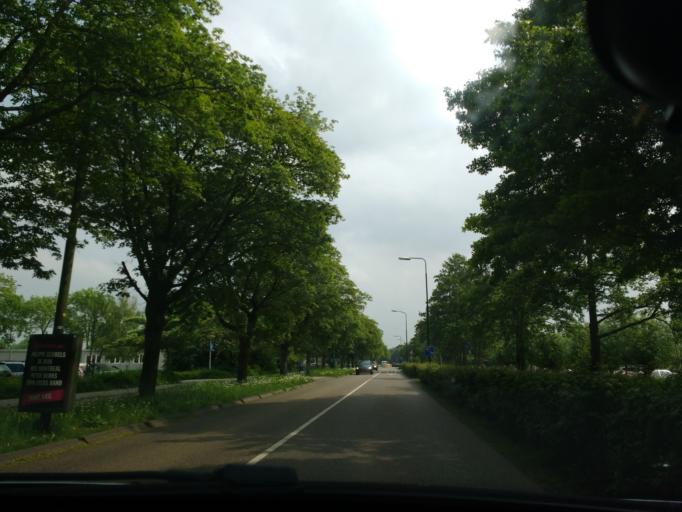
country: NL
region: North Holland
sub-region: Gemeente Naarden
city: Naarden
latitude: 52.2912
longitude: 5.1683
